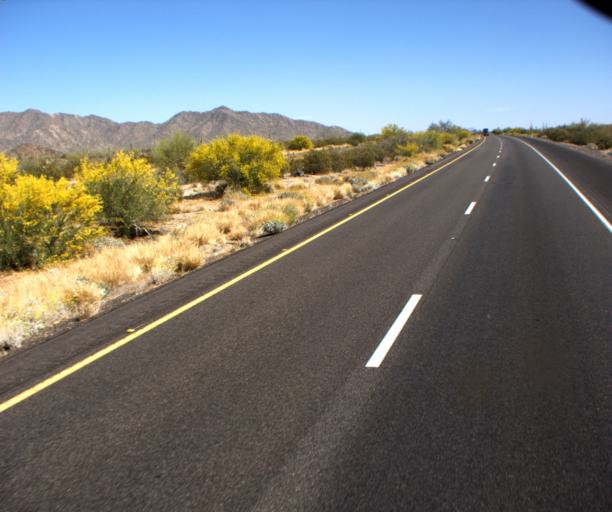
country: US
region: Arizona
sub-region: Maricopa County
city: Gila Bend
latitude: 32.8734
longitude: -112.4430
